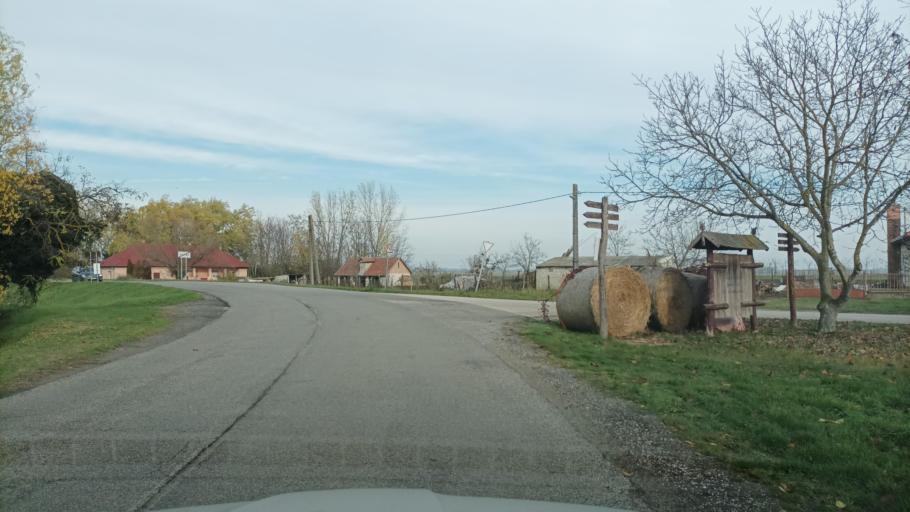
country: HU
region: Fejer
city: Adony
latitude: 47.0952
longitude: 18.9274
